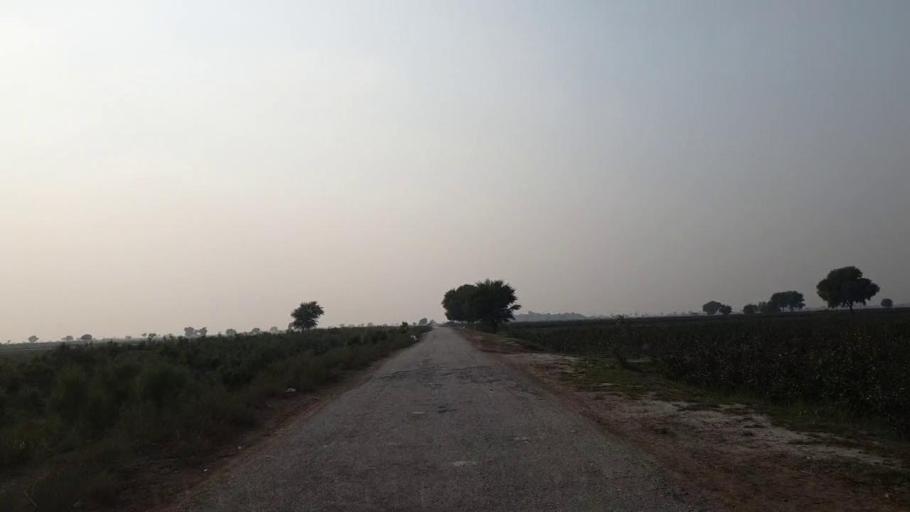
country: PK
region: Sindh
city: Bhan
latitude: 26.4885
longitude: 67.7171
